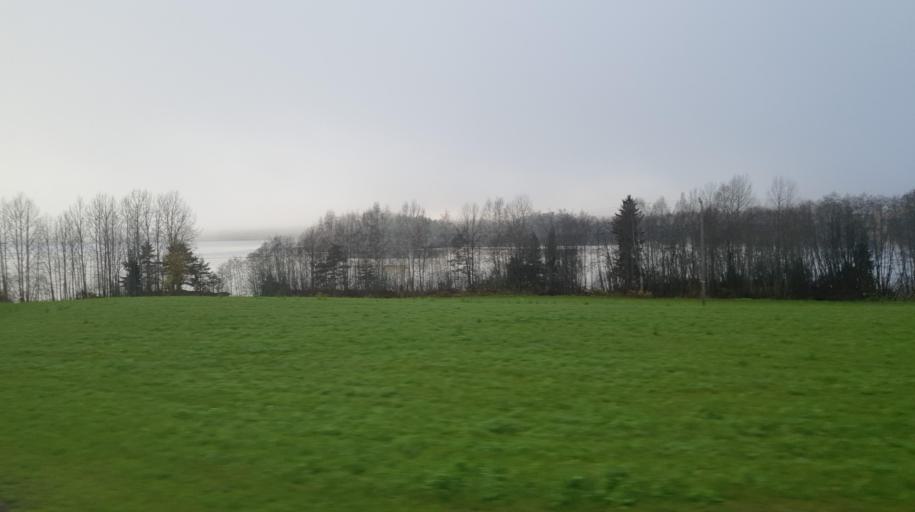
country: NO
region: Buskerud
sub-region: Krodsherad
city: Noresund
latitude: 60.1454
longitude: 9.7665
